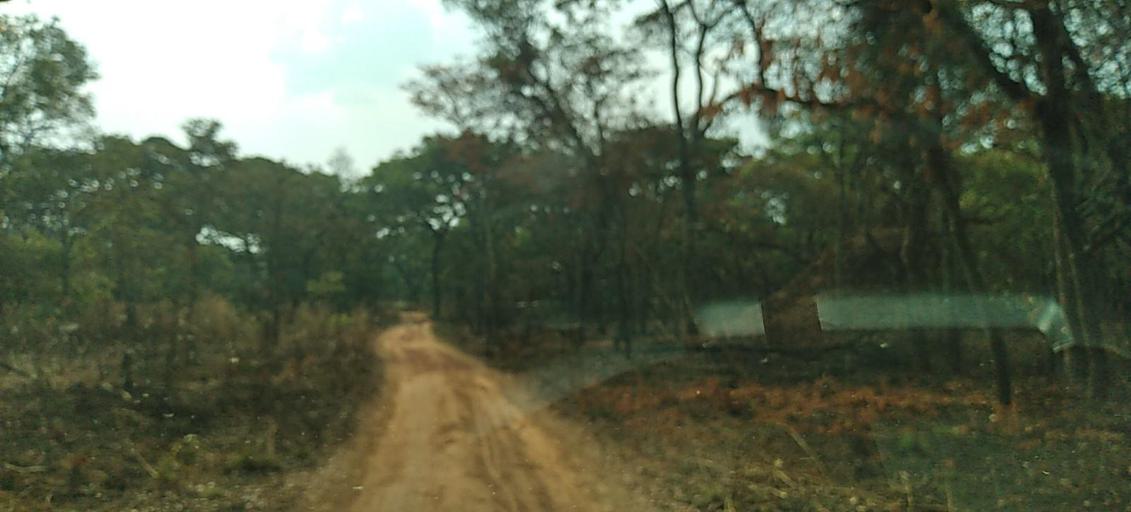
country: ZM
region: North-Western
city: Solwezi
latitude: -12.0690
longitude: 26.2227
